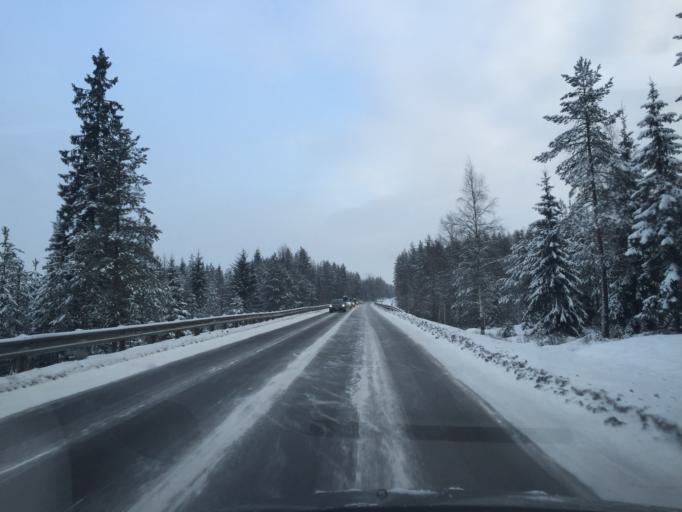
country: NO
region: Hedmark
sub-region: Elverum
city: Elverum
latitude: 60.9548
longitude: 11.7029
